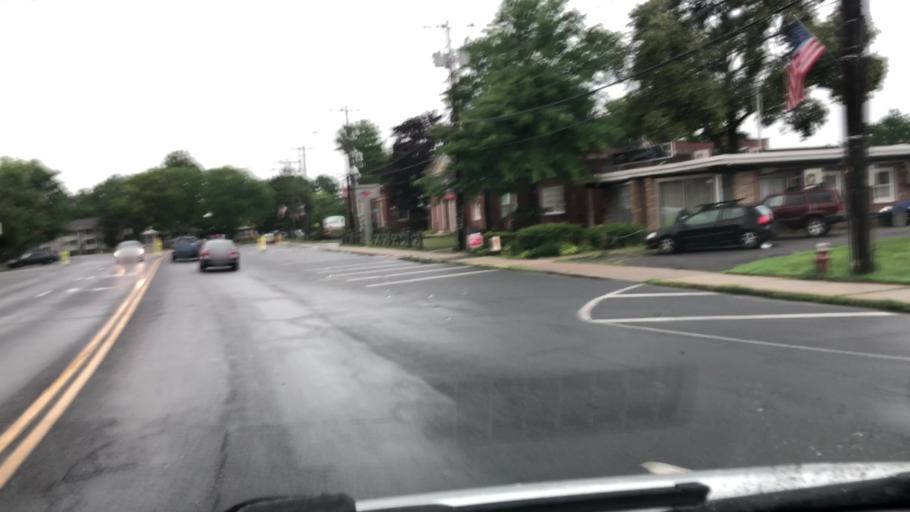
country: US
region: Massachusetts
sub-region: Hampshire County
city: Easthampton
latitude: 42.2705
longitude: -72.6723
